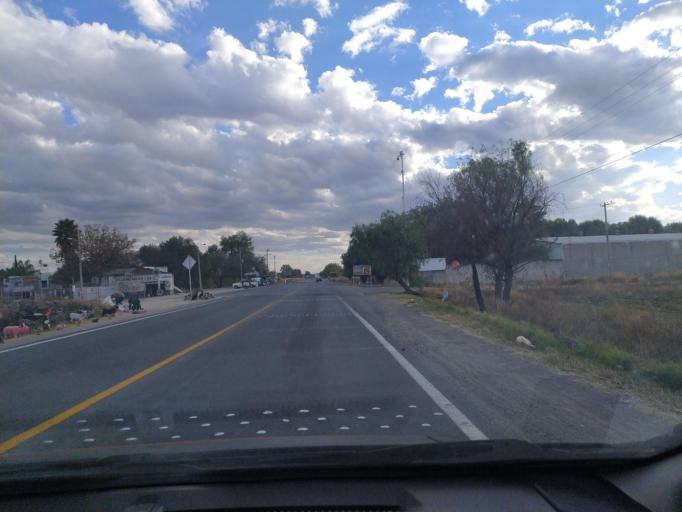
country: LA
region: Oudomxai
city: Muang La
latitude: 21.0216
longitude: 101.8263
